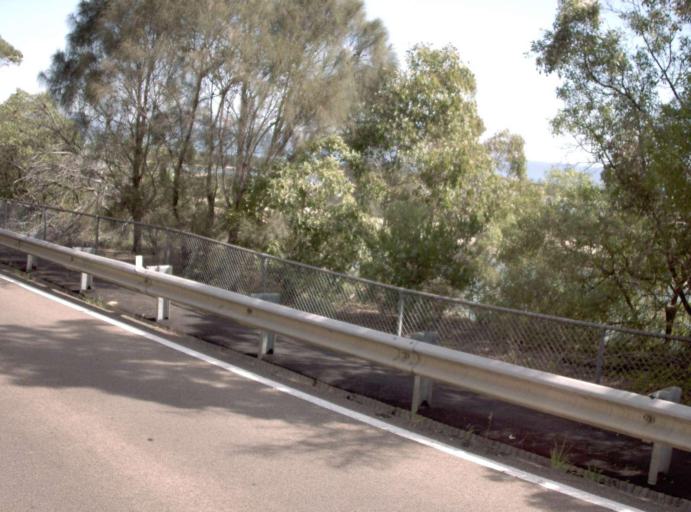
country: AU
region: Victoria
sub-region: East Gippsland
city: Lakes Entrance
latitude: -37.8802
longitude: 147.9629
